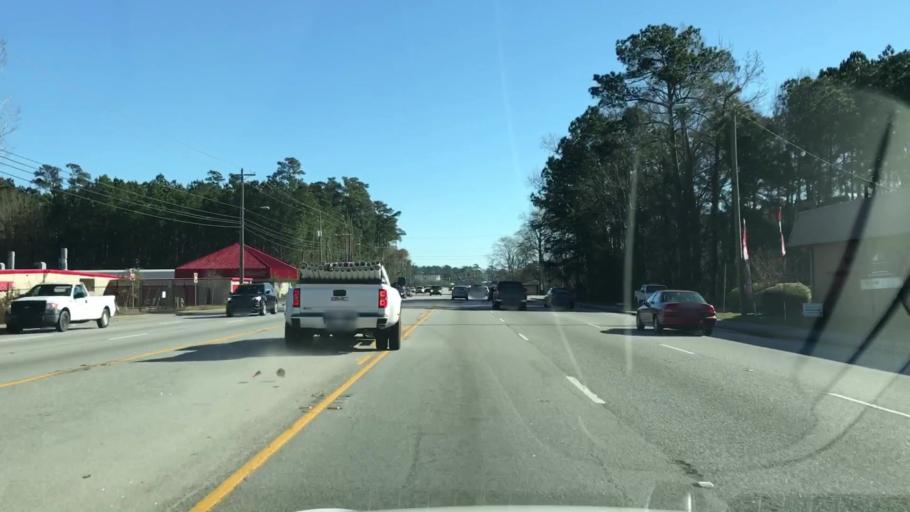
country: US
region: South Carolina
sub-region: Berkeley County
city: Hanahan
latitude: 32.9300
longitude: -80.0702
